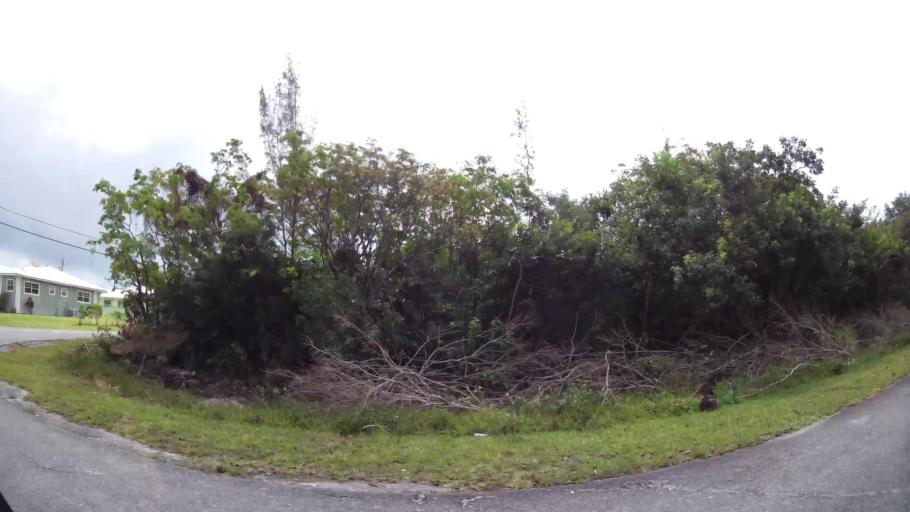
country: BS
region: Freeport
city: Lucaya
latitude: 26.5420
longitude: -78.5967
